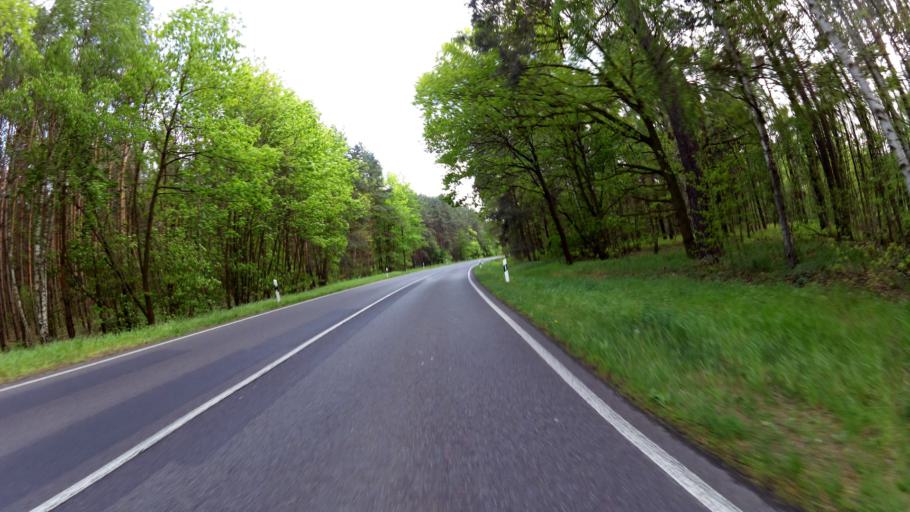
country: DE
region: Brandenburg
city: Storkow
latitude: 52.3069
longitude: 13.9024
